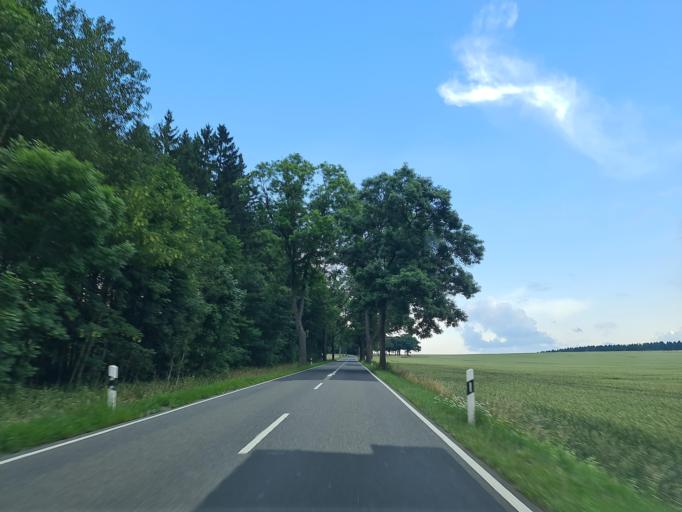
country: DE
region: Saxony
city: Neustadt Vogtland
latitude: 50.4576
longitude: 12.3103
